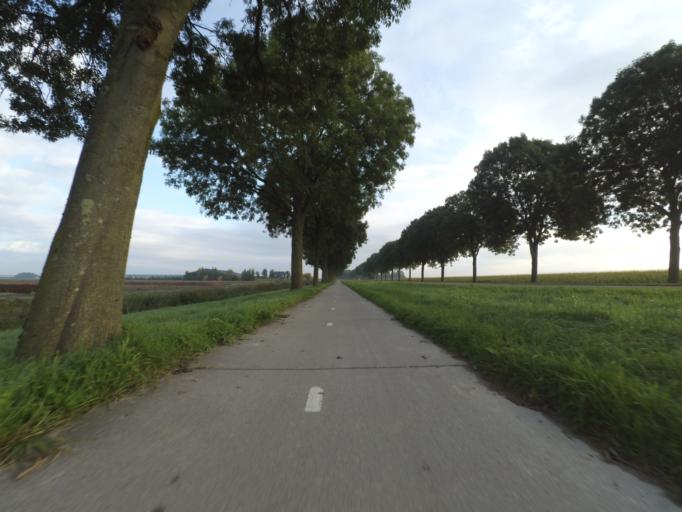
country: NL
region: Flevoland
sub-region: Gemeente Dronten
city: Biddinghuizen
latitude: 52.4905
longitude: 5.6720
